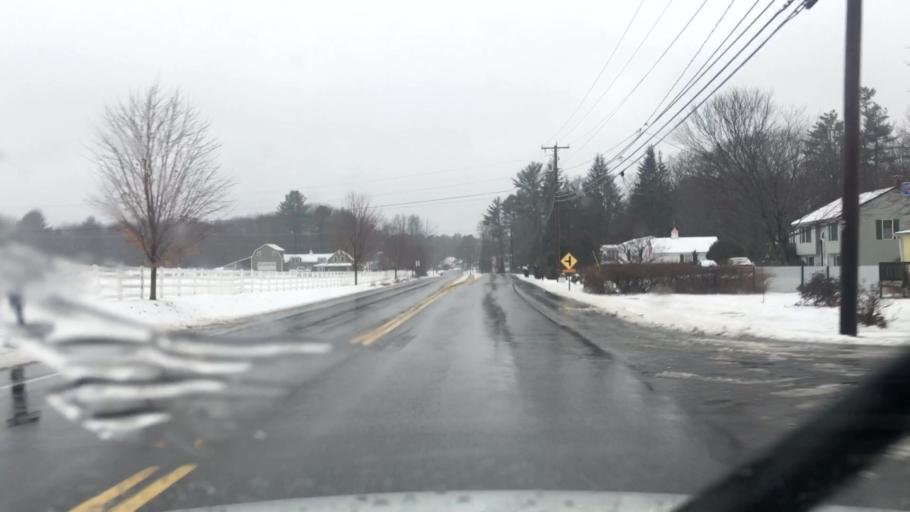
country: US
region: Maine
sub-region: York County
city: Saco
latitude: 43.5429
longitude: -70.4838
